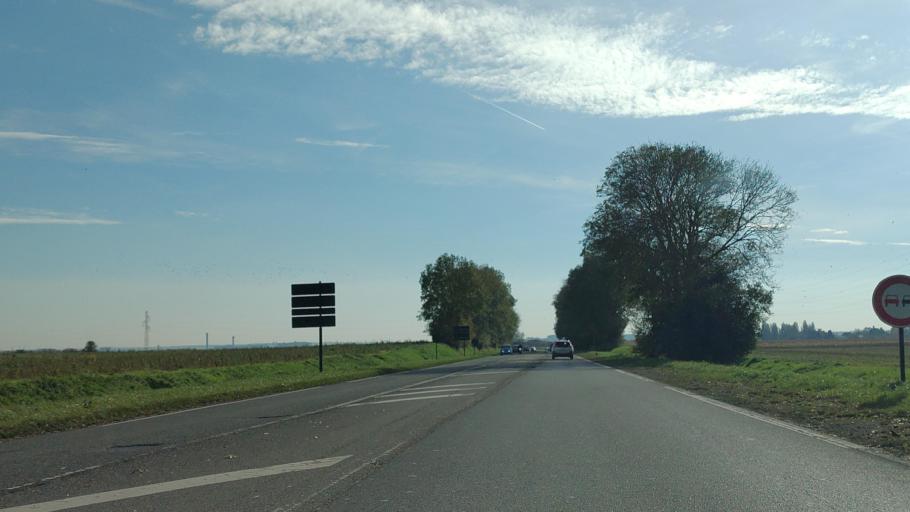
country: FR
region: Ile-de-France
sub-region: Departement du Val-d'Oise
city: Marly-la-Ville
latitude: 49.0757
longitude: 2.5289
